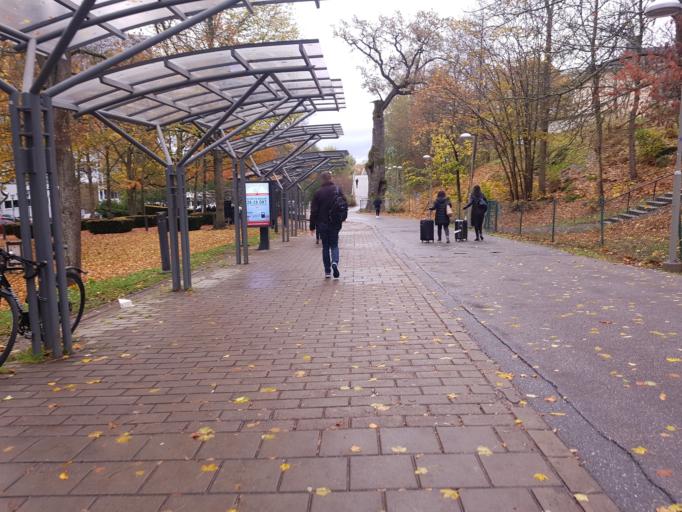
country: SE
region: Stockholm
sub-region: Stockholms Kommun
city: Arsta
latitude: 59.2777
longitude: 18.0123
